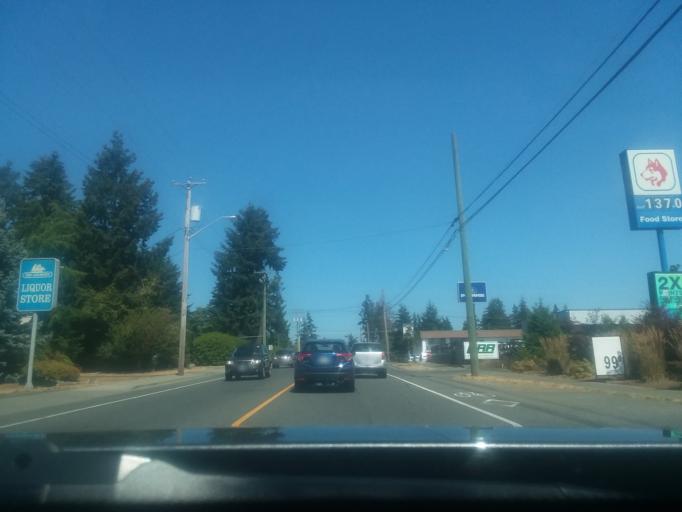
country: CA
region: British Columbia
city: Courtenay
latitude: 49.6864
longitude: -124.9350
